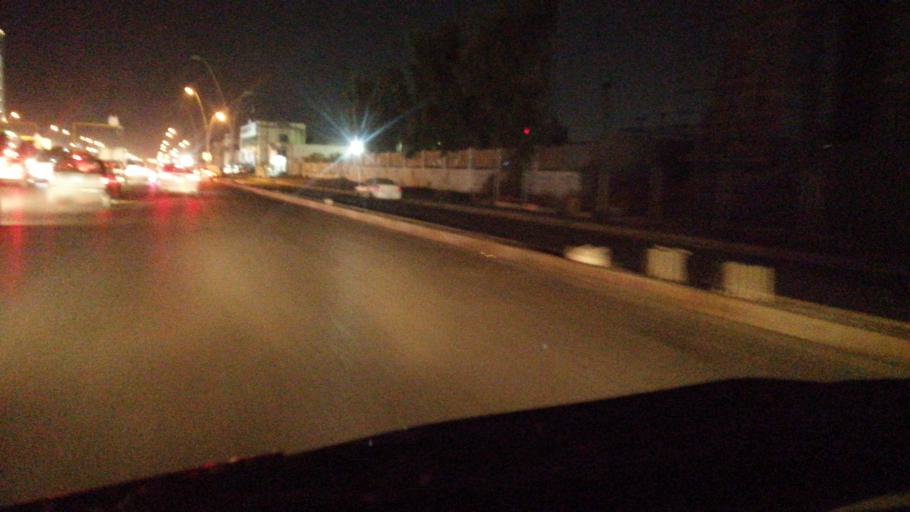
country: IQ
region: Arbil
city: Erbil
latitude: 36.1575
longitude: 43.9855
